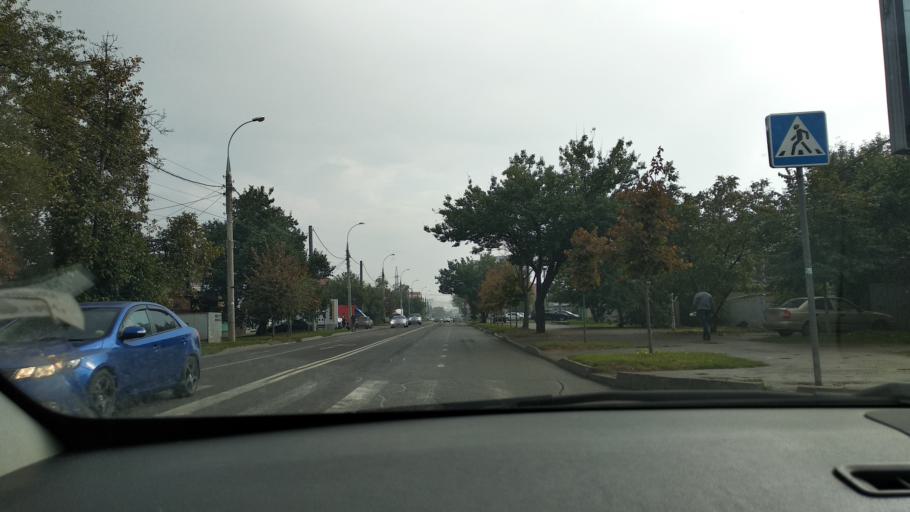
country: RU
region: Krasnodarskiy
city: Krasnodar
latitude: 45.0278
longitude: 39.0223
